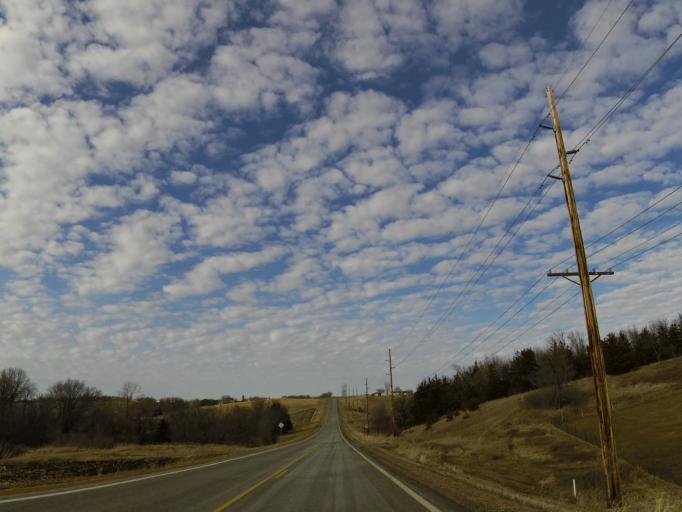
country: US
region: Minnesota
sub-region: Scott County
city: Jordan
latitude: 44.6242
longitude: -93.5628
